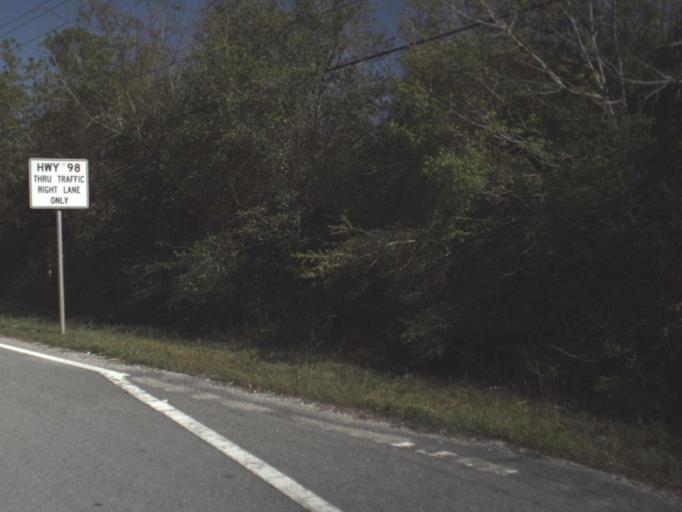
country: US
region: Florida
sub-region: Okaloosa County
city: Mary Esther
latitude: 30.4115
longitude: -86.7171
